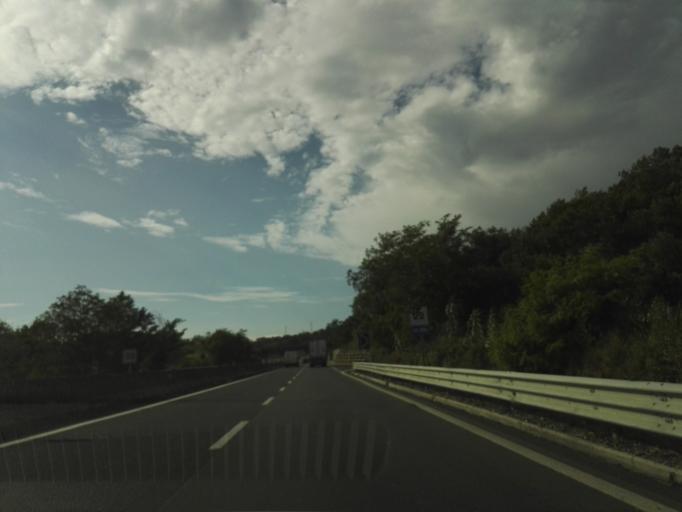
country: IT
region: Calabria
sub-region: Provincia di Catanzaro
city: Marcellinara
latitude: 38.9145
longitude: 16.4925
